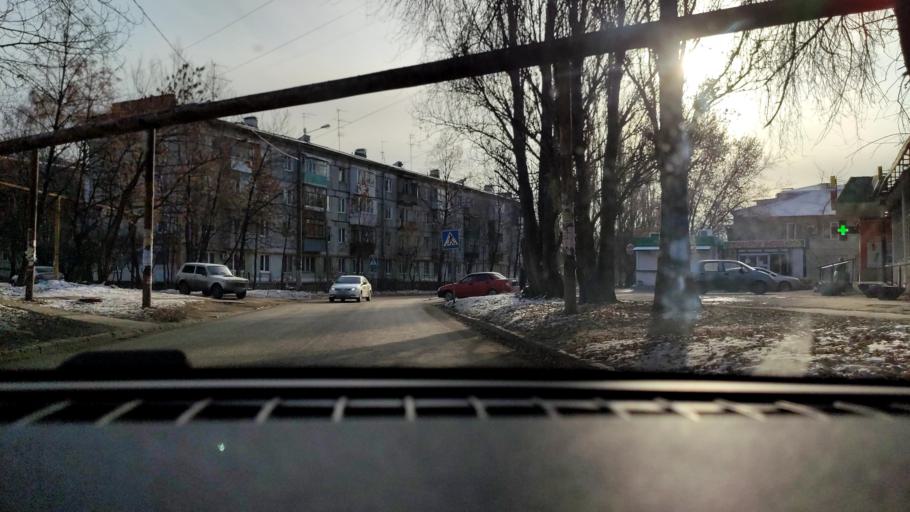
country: RU
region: Samara
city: Petra-Dubrava
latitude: 53.2997
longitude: 50.2812
